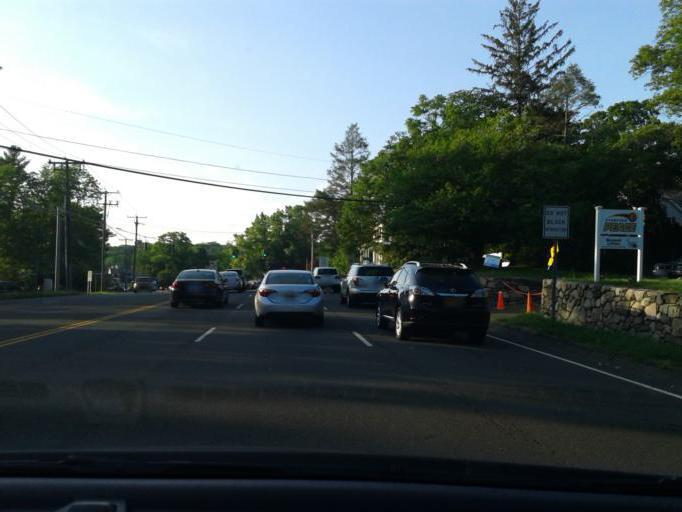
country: US
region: Connecticut
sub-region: Fairfield County
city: North Stamford
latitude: 41.1005
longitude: -73.5648
